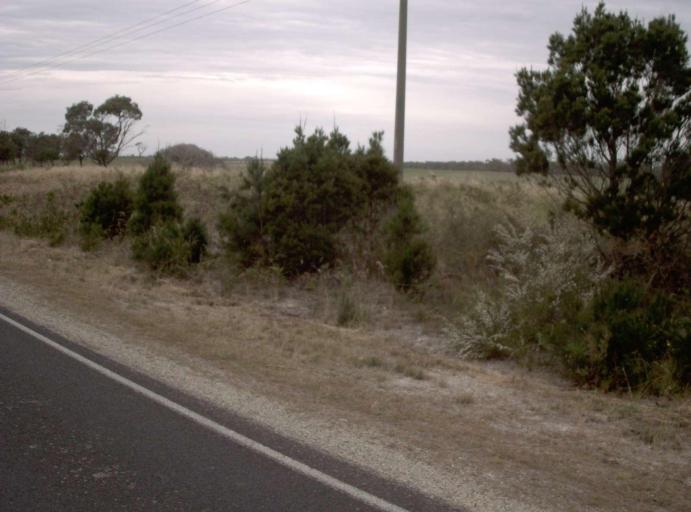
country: AU
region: Victoria
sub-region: Wellington
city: Sale
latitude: -38.2012
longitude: 147.3257
